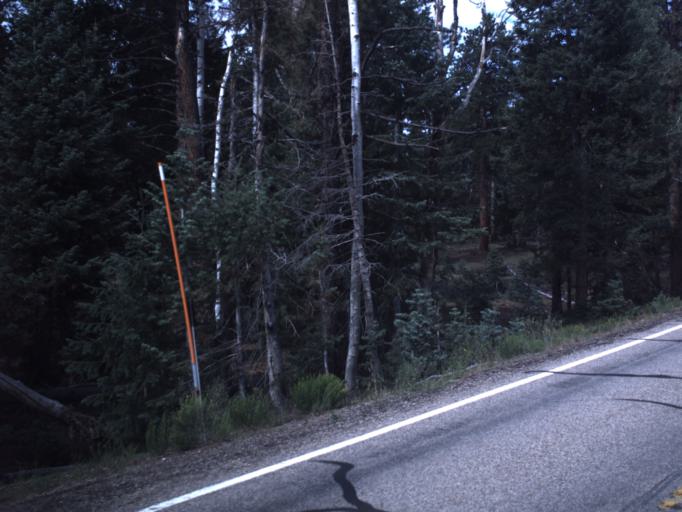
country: US
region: Utah
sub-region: Garfield County
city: Panguitch
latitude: 37.5142
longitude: -112.6383
